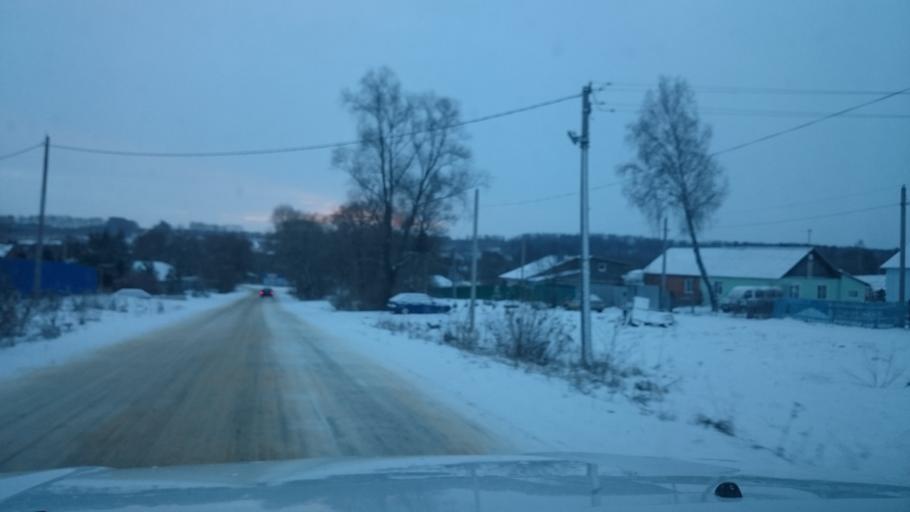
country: RU
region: Tula
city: Leninskiy
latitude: 54.2460
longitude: 37.2579
